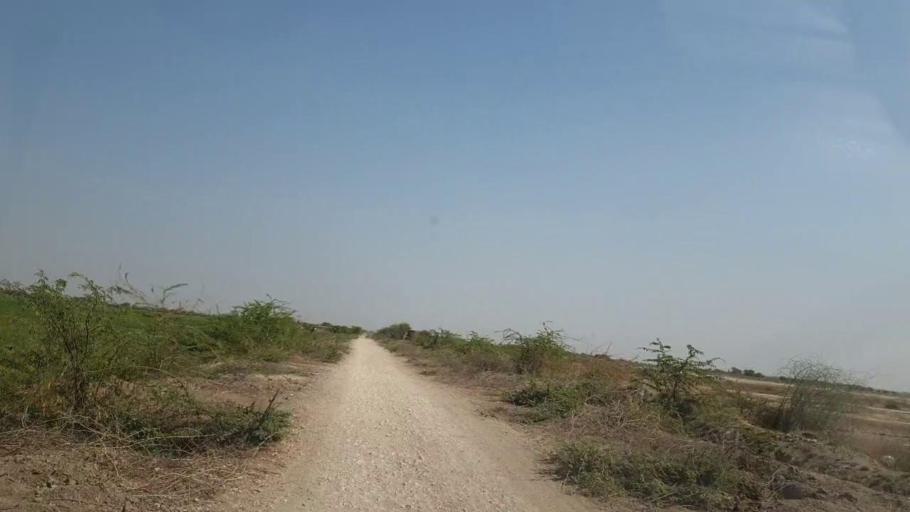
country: PK
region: Sindh
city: Nabisar
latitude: 25.0750
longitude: 69.5511
